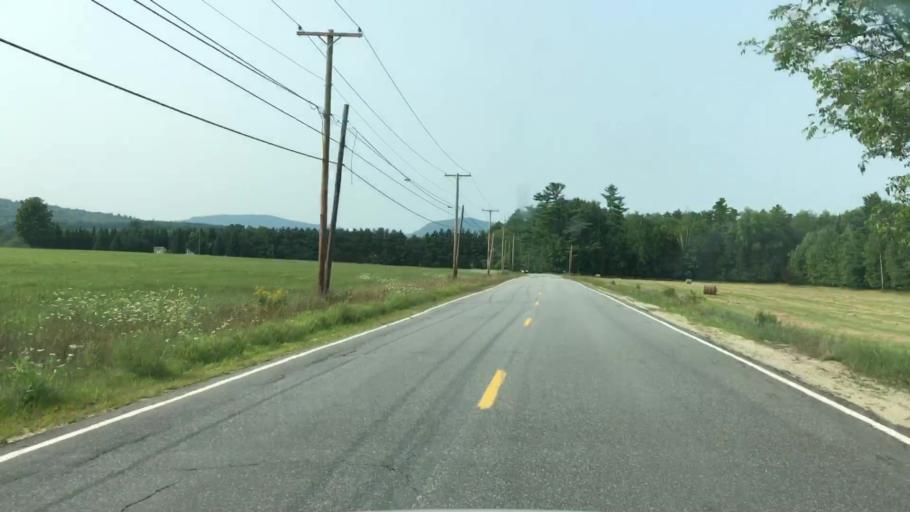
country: US
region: Maine
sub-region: Oxford County
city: Norway
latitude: 44.2274
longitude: -70.5947
